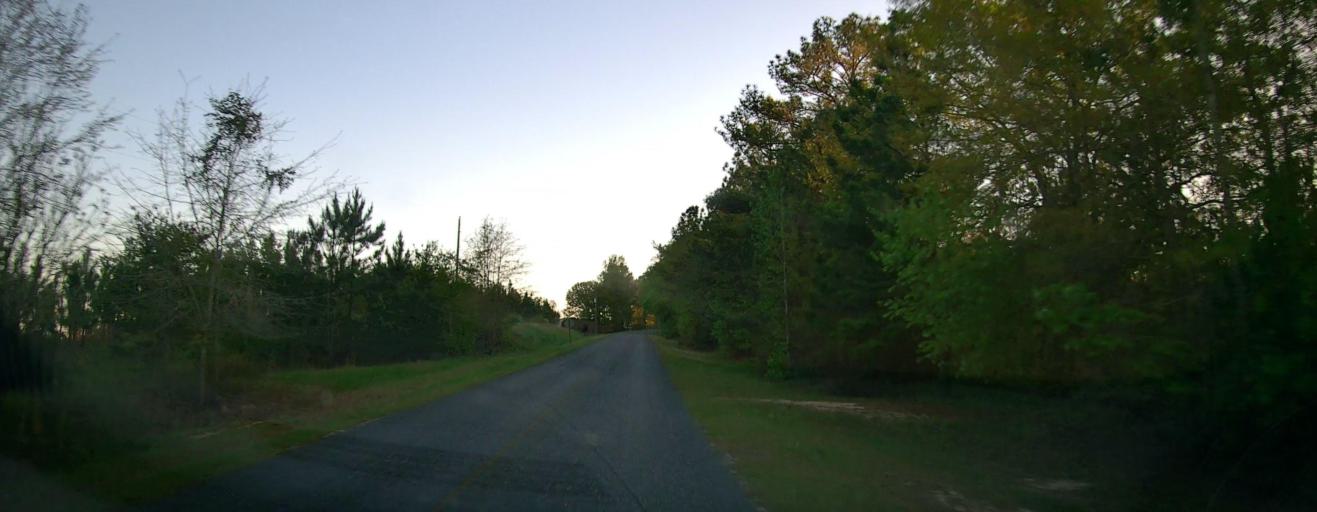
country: US
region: Georgia
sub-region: Talbot County
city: Talbotton
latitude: 32.5416
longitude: -84.5712
